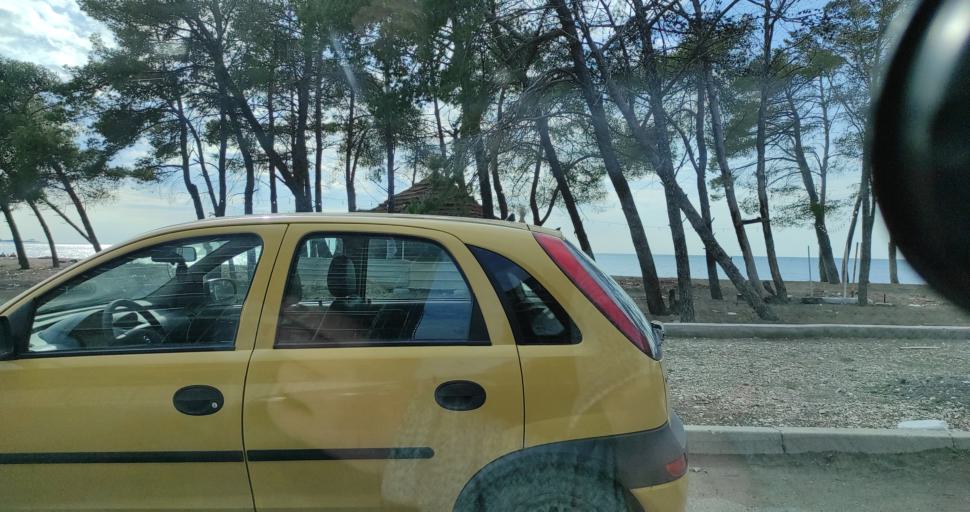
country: AL
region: Lezhe
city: Shengjin
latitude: 41.7924
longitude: 19.6028
